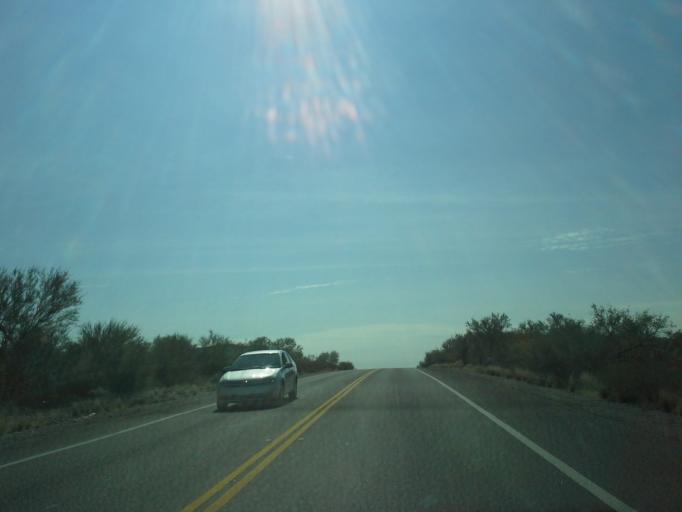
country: US
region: Arizona
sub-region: Pima County
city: Flowing Wells
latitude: 32.2344
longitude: -111.0212
